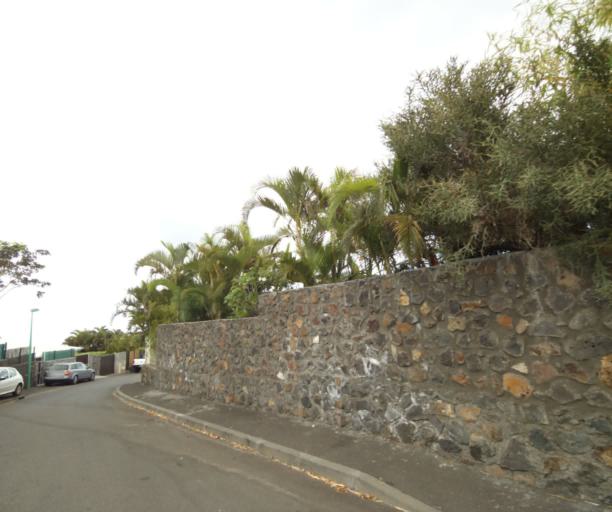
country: RE
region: Reunion
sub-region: Reunion
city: Saint-Paul
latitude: -21.0624
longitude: 55.2255
